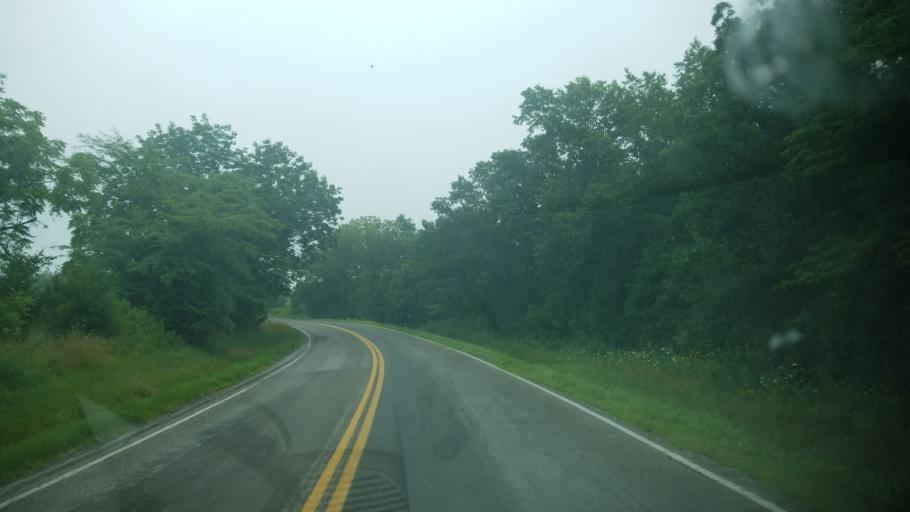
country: US
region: Missouri
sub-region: Audrain County
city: Vandalia
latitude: 39.3058
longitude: -91.3458
